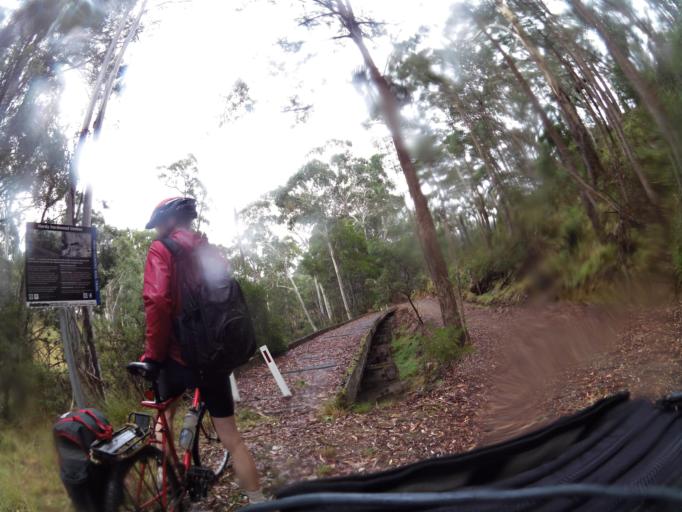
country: AU
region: New South Wales
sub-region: Greater Hume Shire
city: Holbrook
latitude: -36.1674
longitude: 147.4858
